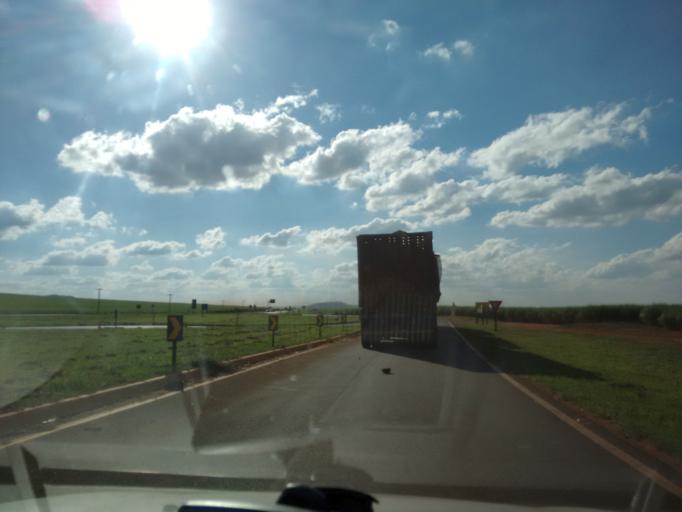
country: BR
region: Sao Paulo
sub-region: Americo Brasiliense
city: Americo Brasiliense
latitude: -21.6138
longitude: -48.0315
